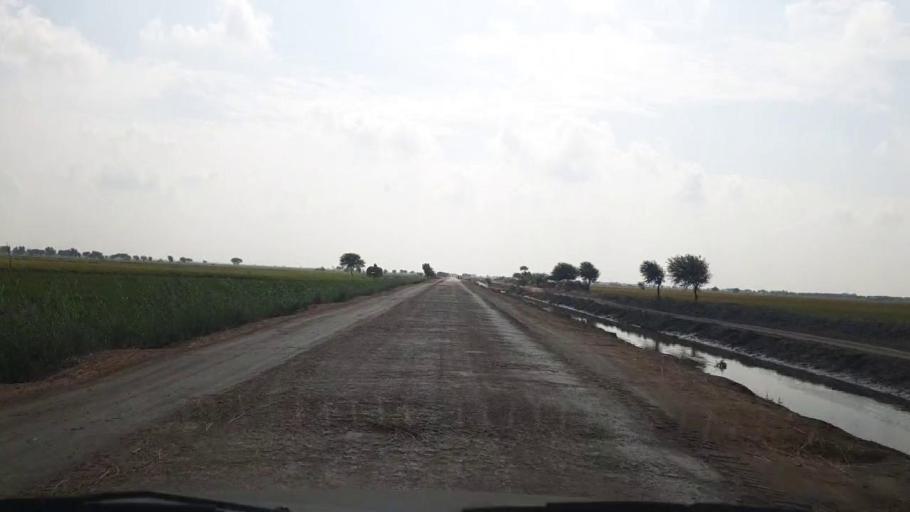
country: PK
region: Sindh
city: Kario
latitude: 24.5866
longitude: 68.5753
